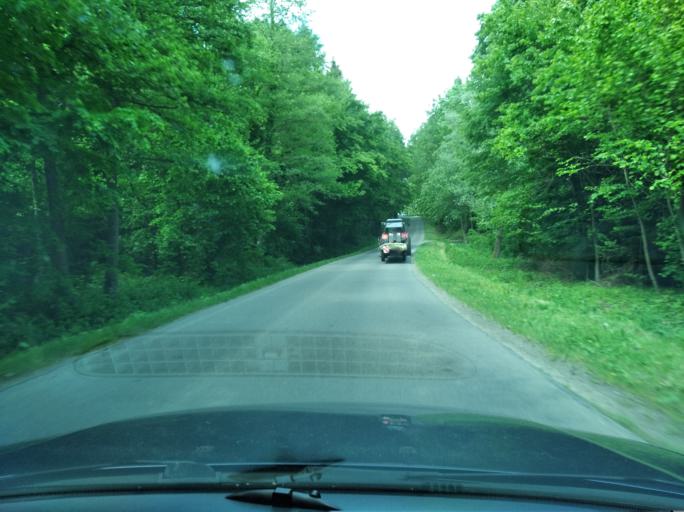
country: PL
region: Subcarpathian Voivodeship
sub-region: Powiat ropczycko-sedziszowski
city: Ropczyce
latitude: 50.0184
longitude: 21.6084
